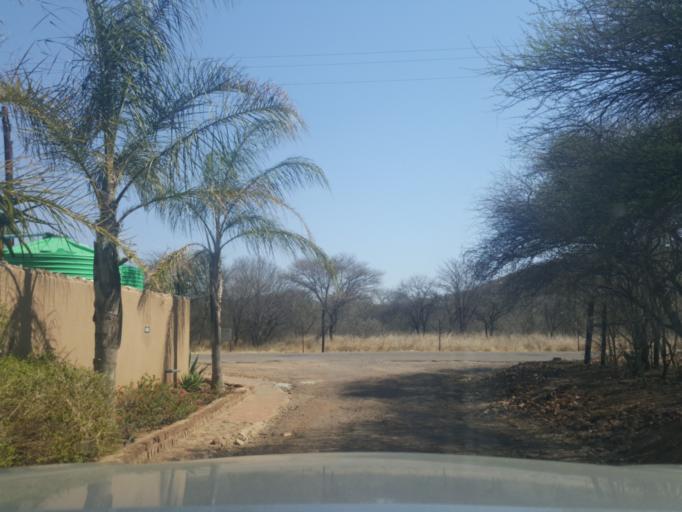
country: BW
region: Kweneng
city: Gabane
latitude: -24.7440
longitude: 25.8283
